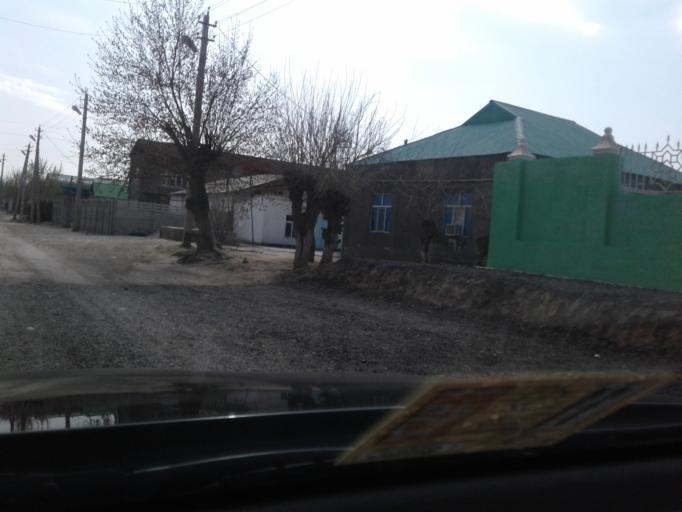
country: TM
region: Ahal
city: Abadan
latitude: 38.1210
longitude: 58.3489
